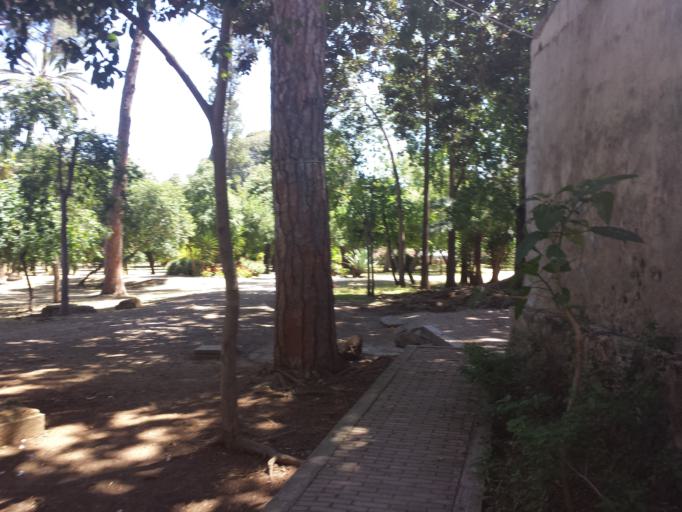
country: IT
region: Sicily
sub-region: Palermo
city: Palermo
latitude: 38.1308
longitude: 13.3456
